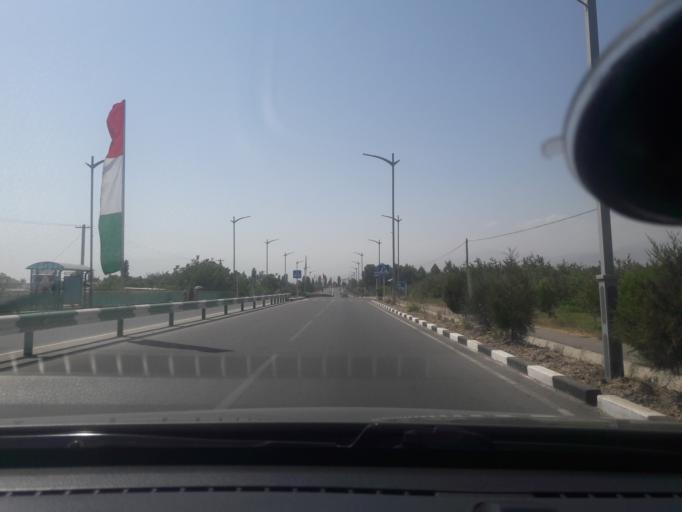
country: TJ
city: Shahrinav
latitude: 38.5641
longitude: 68.4018
